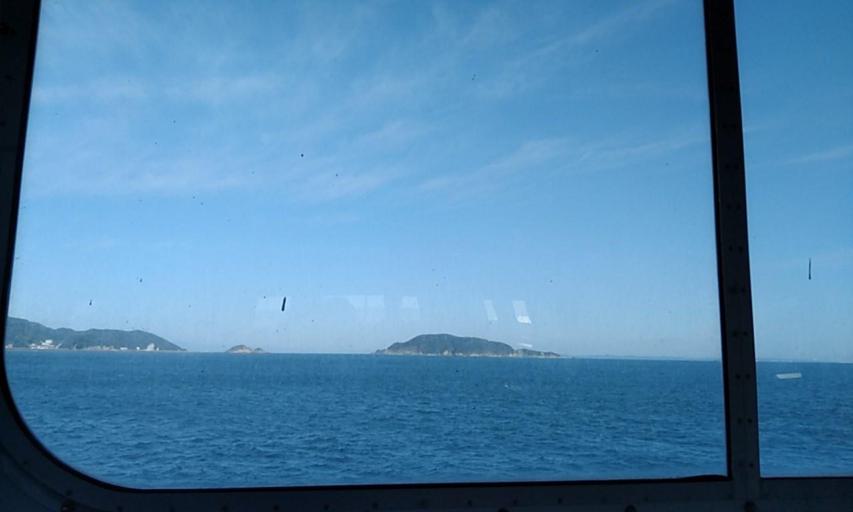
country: JP
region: Mie
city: Toba
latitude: 34.5171
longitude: 136.9198
